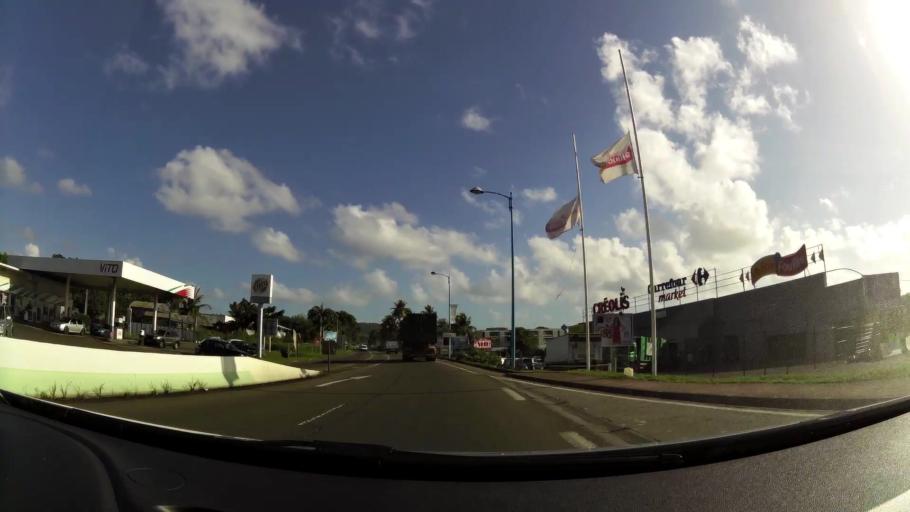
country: MQ
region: Martinique
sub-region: Martinique
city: Le Robert
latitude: 14.6751
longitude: -60.9463
